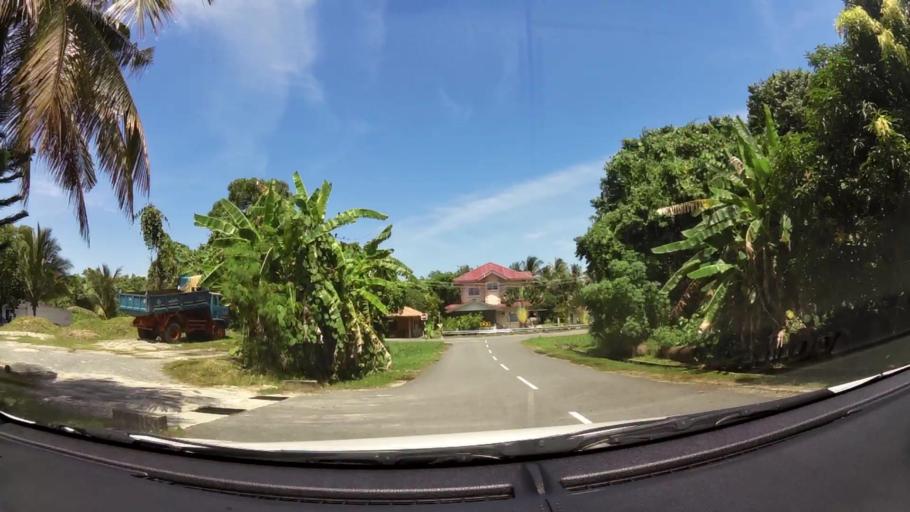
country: BN
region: Brunei and Muara
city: Bandar Seri Begawan
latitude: 4.9370
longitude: 114.9539
